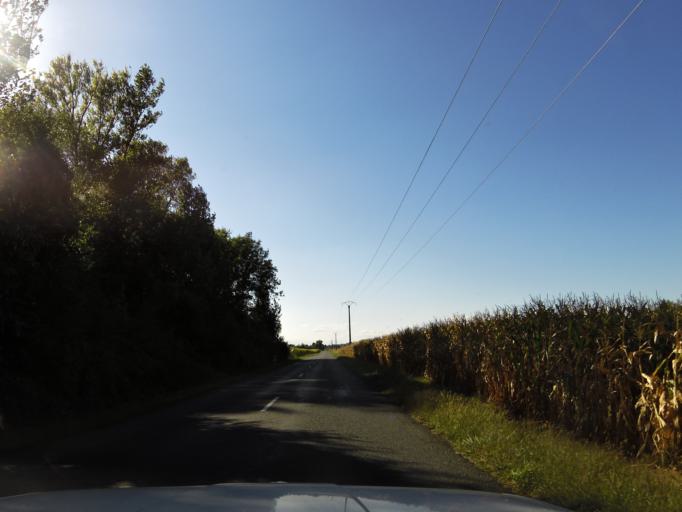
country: FR
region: Rhone-Alpes
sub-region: Departement de l'Ain
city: Leyment
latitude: 45.8827
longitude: 5.3002
